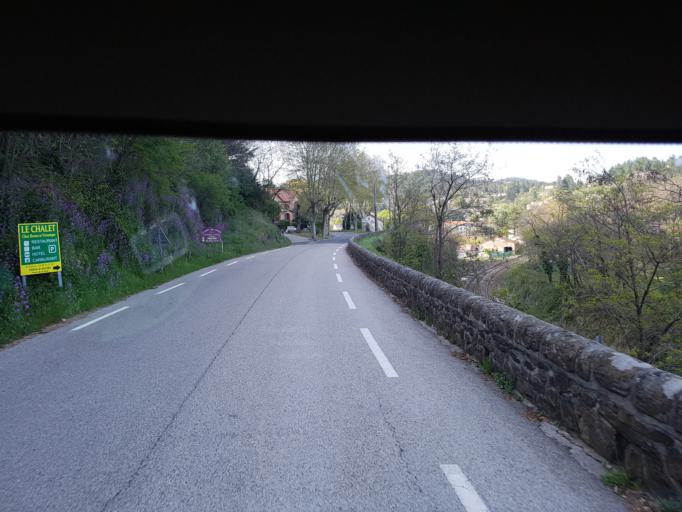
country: FR
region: Languedoc-Roussillon
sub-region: Departement du Gard
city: Branoux-les-Taillades
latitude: 44.3446
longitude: 3.9507
